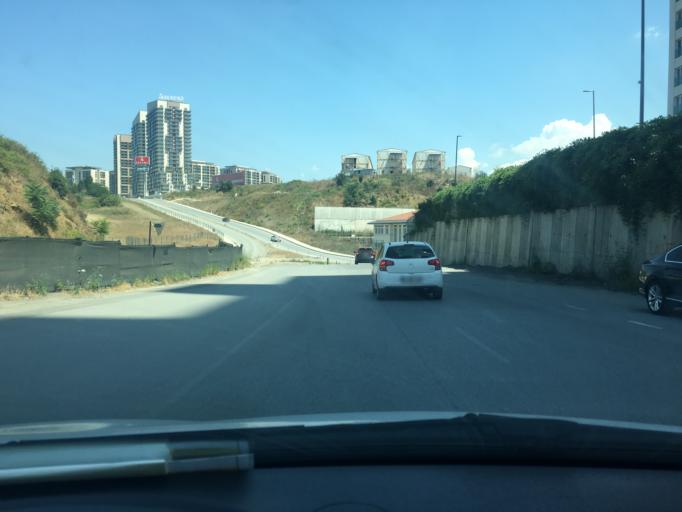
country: TR
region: Istanbul
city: Sisli
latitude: 41.0910
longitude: 28.9387
